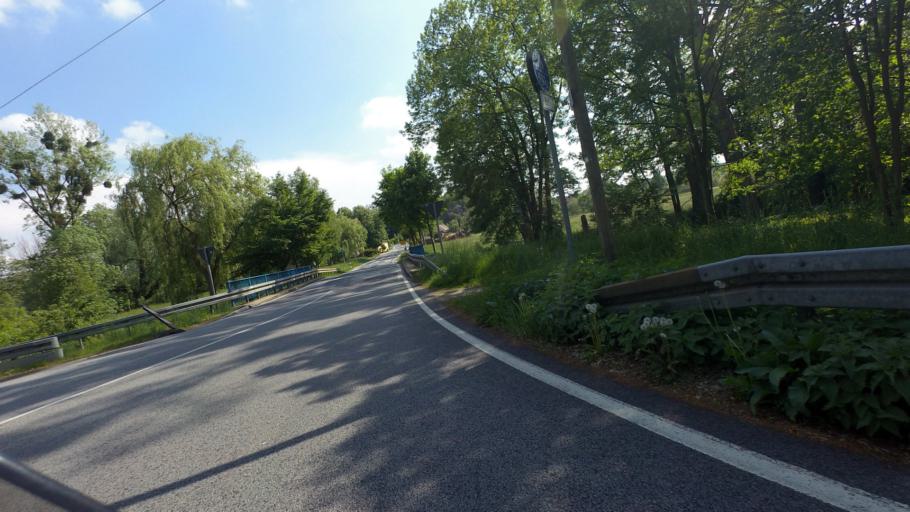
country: DE
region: Saxony
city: Weissenberg
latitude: 51.1914
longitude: 14.6780
